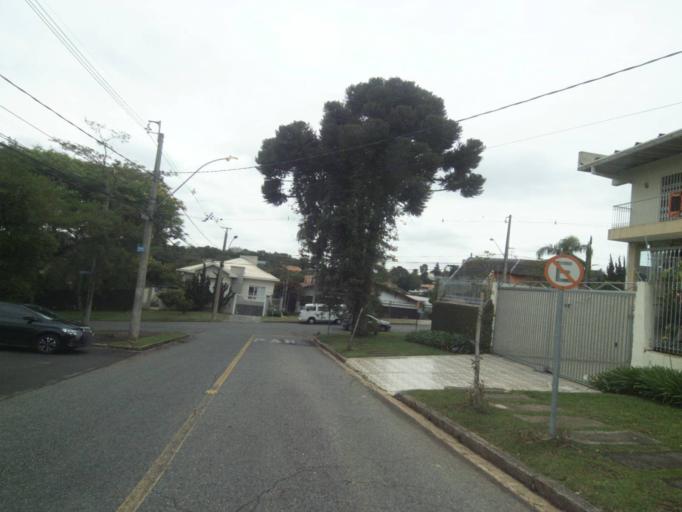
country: BR
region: Parana
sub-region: Curitiba
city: Curitiba
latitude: -25.4070
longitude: -49.2862
